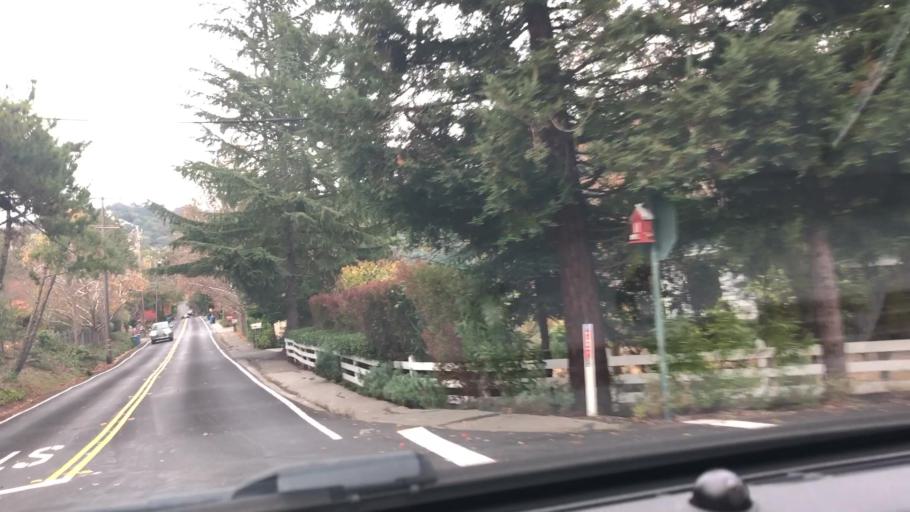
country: US
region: California
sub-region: Contra Costa County
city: Lafayette
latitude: 37.8998
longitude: -122.1509
